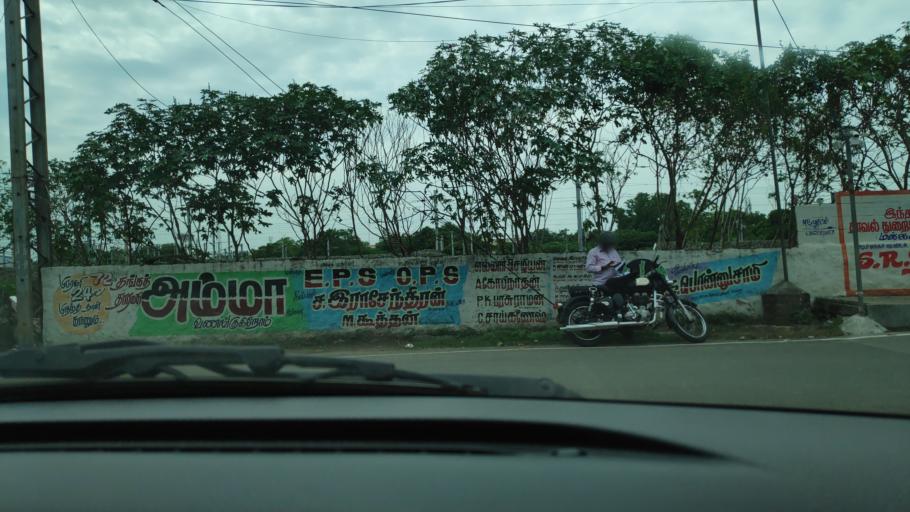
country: IN
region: Tamil Nadu
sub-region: Kancheepuram
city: Pallavaram
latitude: 12.9340
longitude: 80.1296
